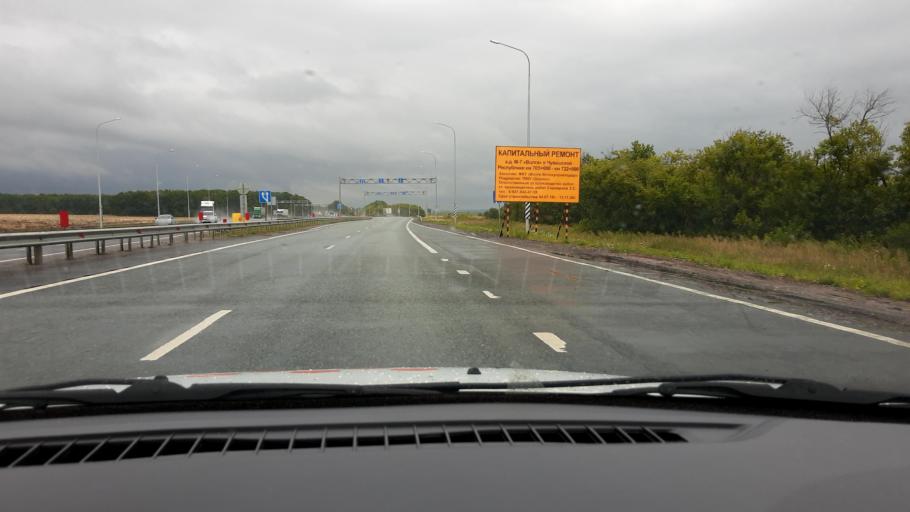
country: RU
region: Chuvashia
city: Yantikovo
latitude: 55.7952
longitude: 47.8256
